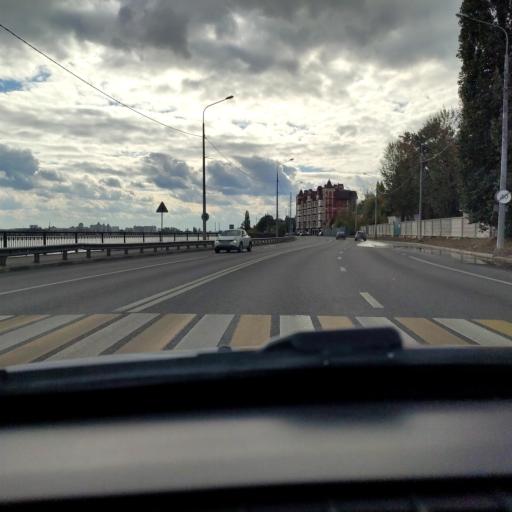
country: RU
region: Voronezj
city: Voronezh
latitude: 51.6843
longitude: 39.2287
